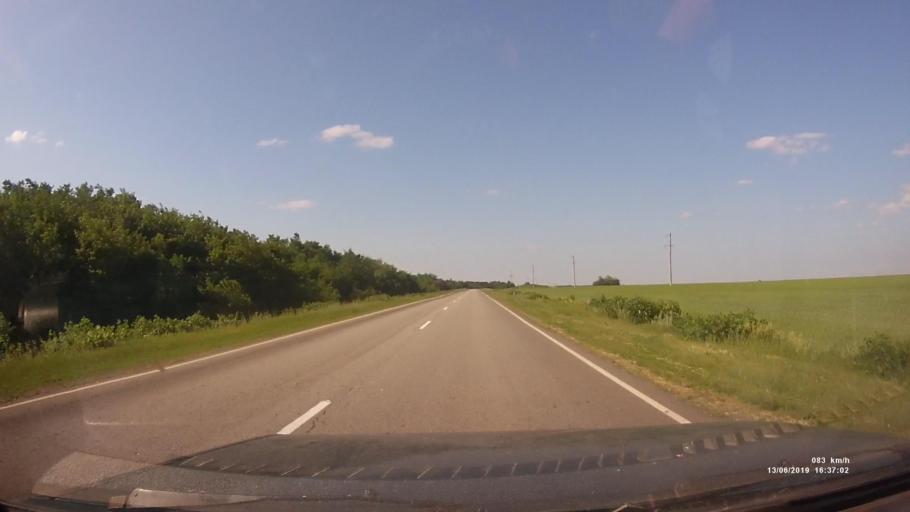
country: RU
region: Rostov
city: Kazanskaya
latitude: 49.9023
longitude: 41.3098
